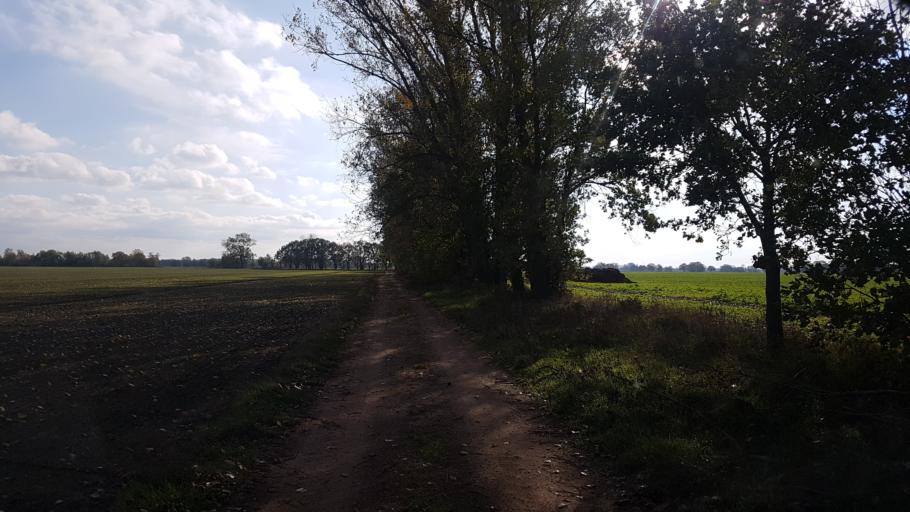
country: DE
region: Brandenburg
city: Schonewalde
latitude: 51.6891
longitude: 13.5765
